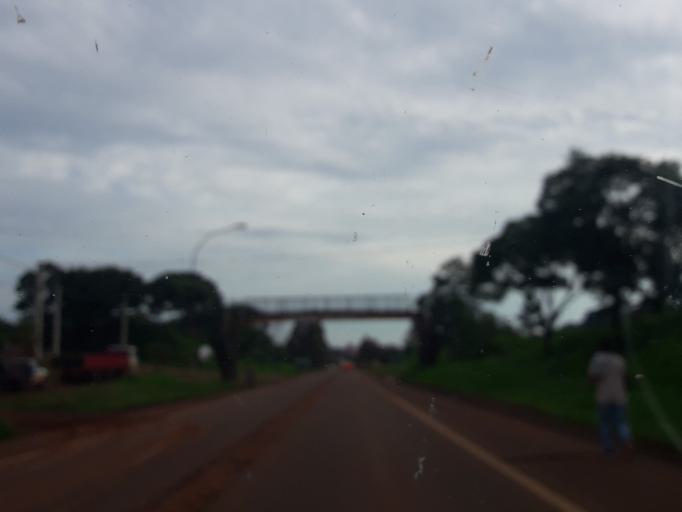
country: AR
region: Misiones
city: Dos de Mayo
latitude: -26.9970
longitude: -54.4934
